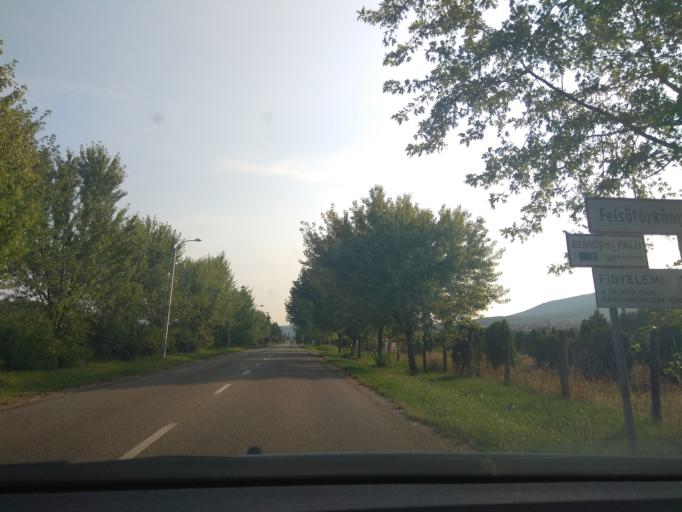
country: HU
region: Heves
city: Felsotarkany
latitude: 47.9599
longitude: 20.3985
